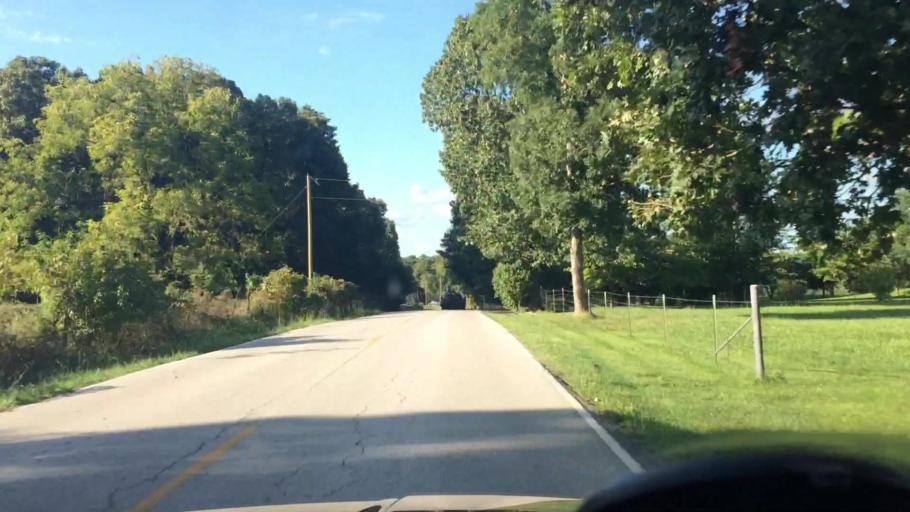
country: US
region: Missouri
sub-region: Greene County
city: Strafford
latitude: 37.2818
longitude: -93.0812
